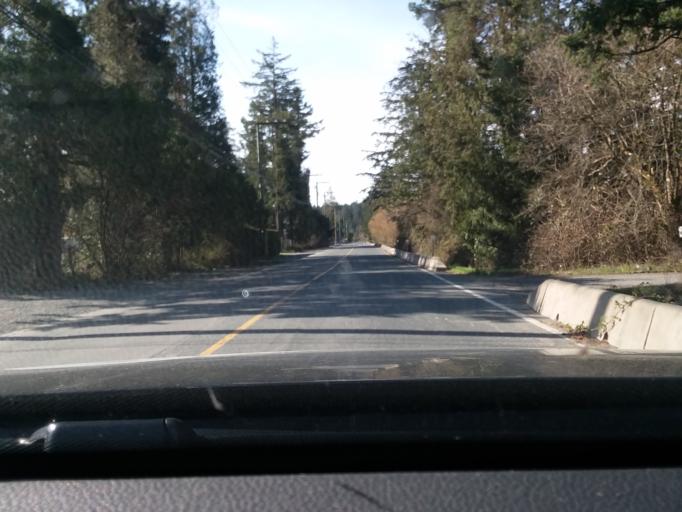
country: CA
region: British Columbia
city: Langford
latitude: 48.4272
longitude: -123.5362
